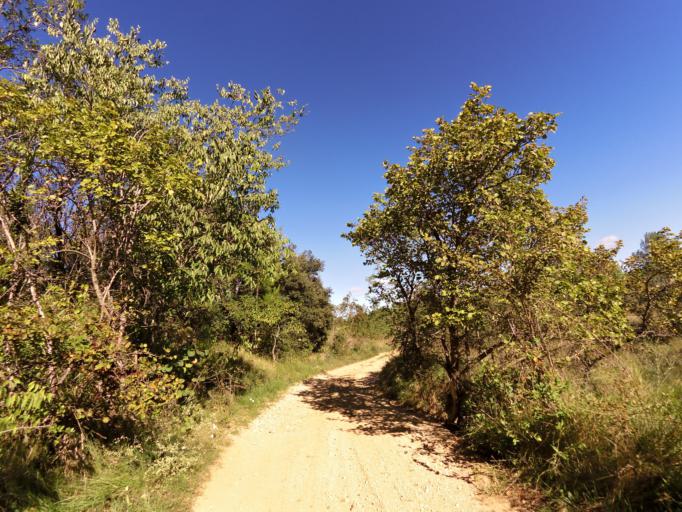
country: FR
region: Languedoc-Roussillon
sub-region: Departement de l'Herault
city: Villetelle
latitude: 43.7379
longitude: 4.1502
